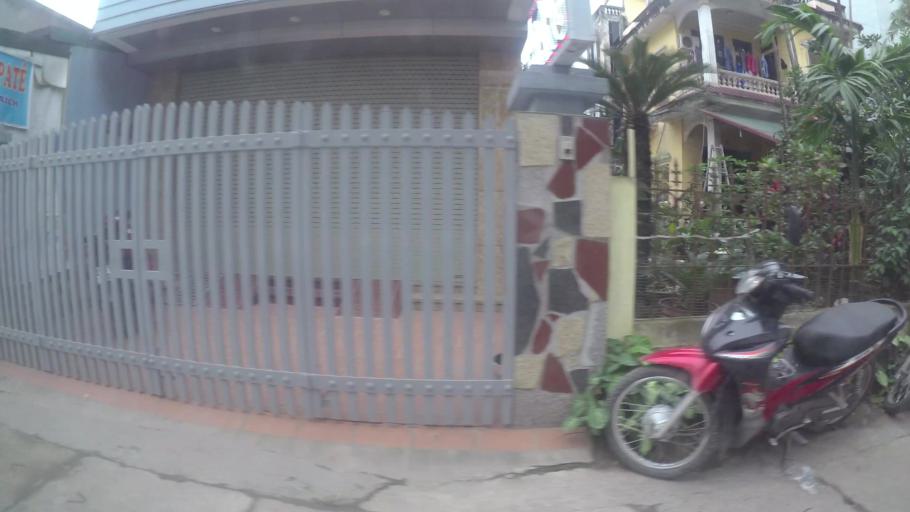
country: VN
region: Ha Noi
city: Tay Ho
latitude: 21.0671
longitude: 105.8326
